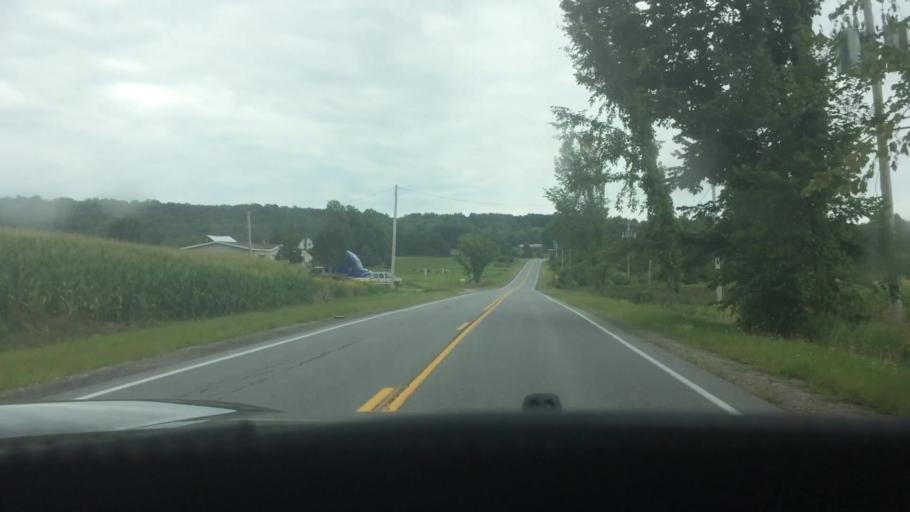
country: US
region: New York
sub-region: St. Lawrence County
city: Canton
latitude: 44.5503
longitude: -75.1065
